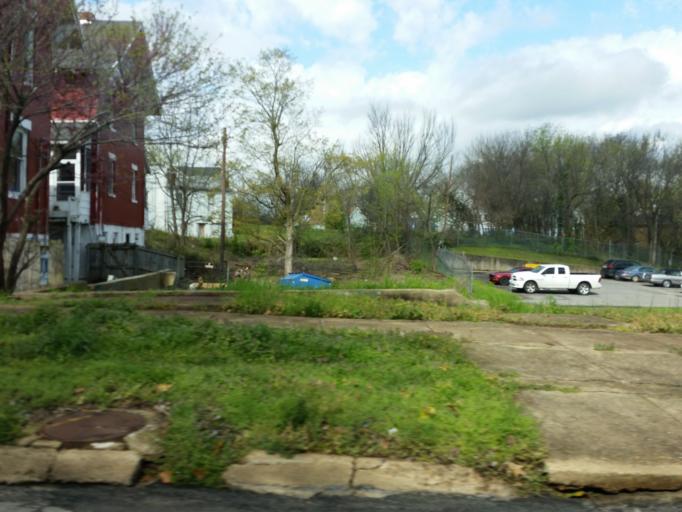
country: US
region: Missouri
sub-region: Butler County
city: Poplar Bluff
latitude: 36.7585
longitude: -90.3914
